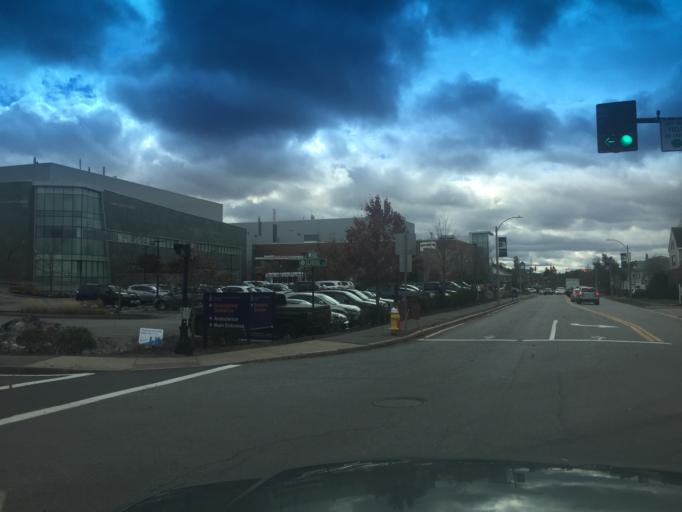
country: US
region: Massachusetts
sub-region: Norfolk County
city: Needham
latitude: 42.2782
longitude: -71.2373
